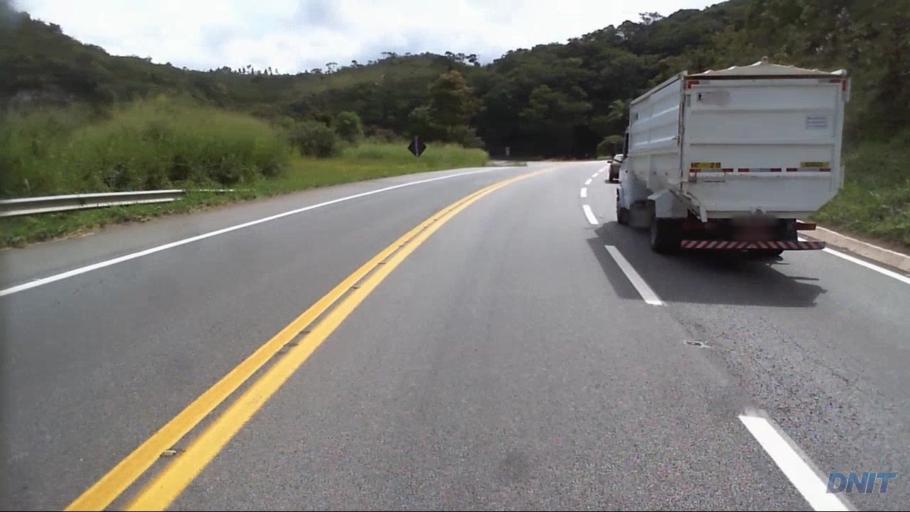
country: BR
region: Minas Gerais
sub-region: Santa Luzia
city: Santa Luzia
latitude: -19.8001
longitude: -43.7593
